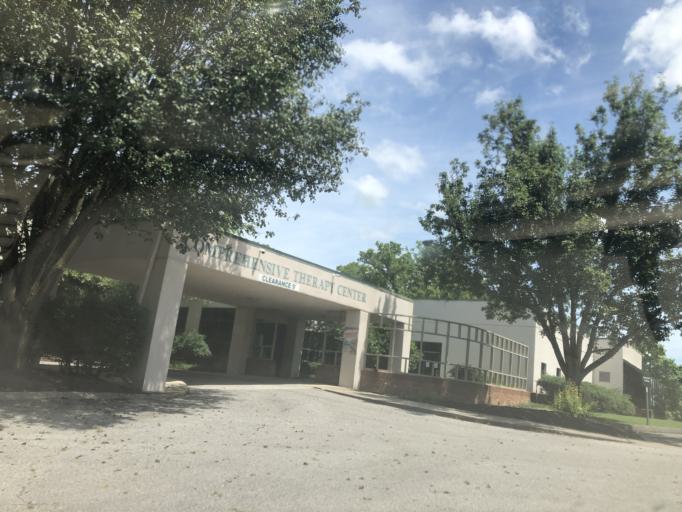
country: US
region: Tennessee
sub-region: Davidson County
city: Lakewood
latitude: 36.2538
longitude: -86.6814
